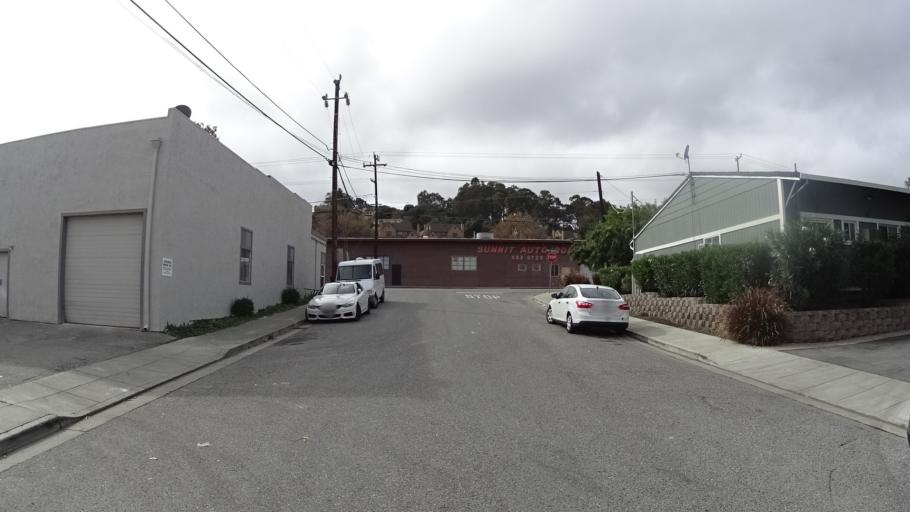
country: US
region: California
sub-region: San Mateo County
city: Belmont
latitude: 37.5270
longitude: -122.2821
